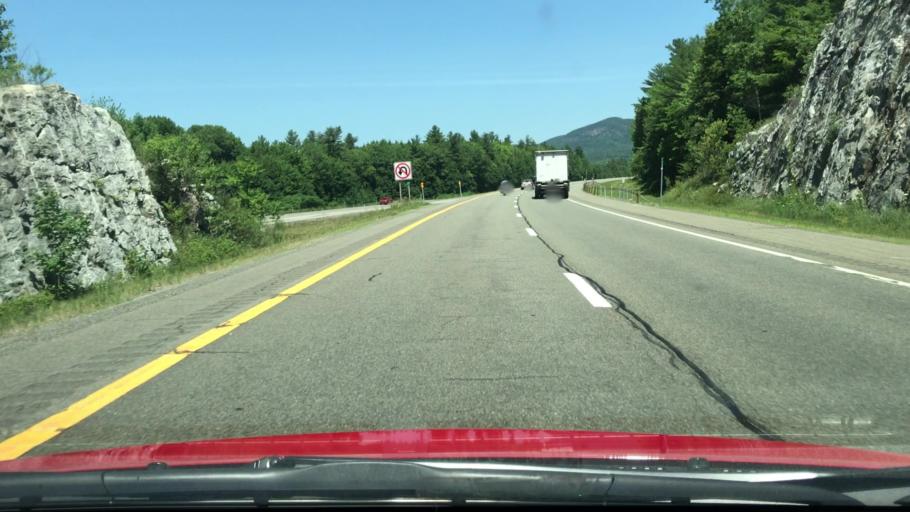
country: US
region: New York
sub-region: Essex County
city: Elizabethtown
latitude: 44.3342
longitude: -73.5331
